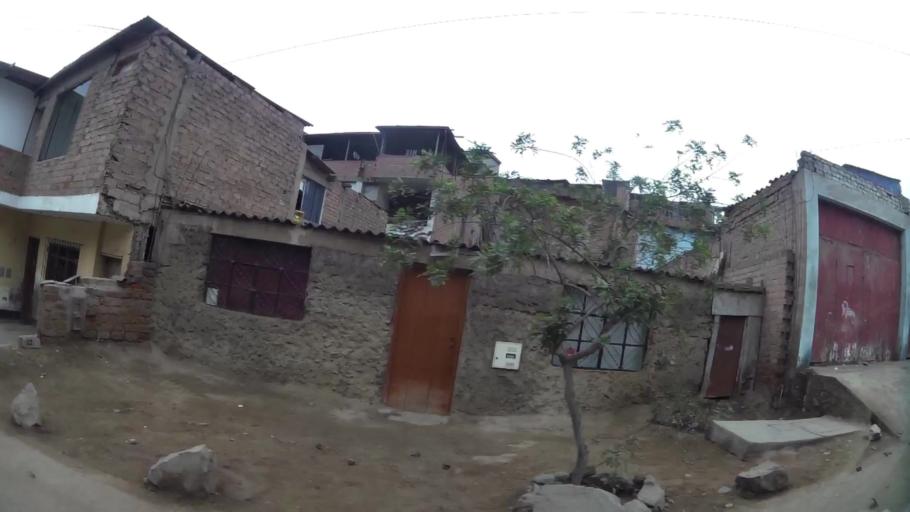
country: PE
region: Lima
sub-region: Lima
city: Surco
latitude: -12.1582
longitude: -76.9497
